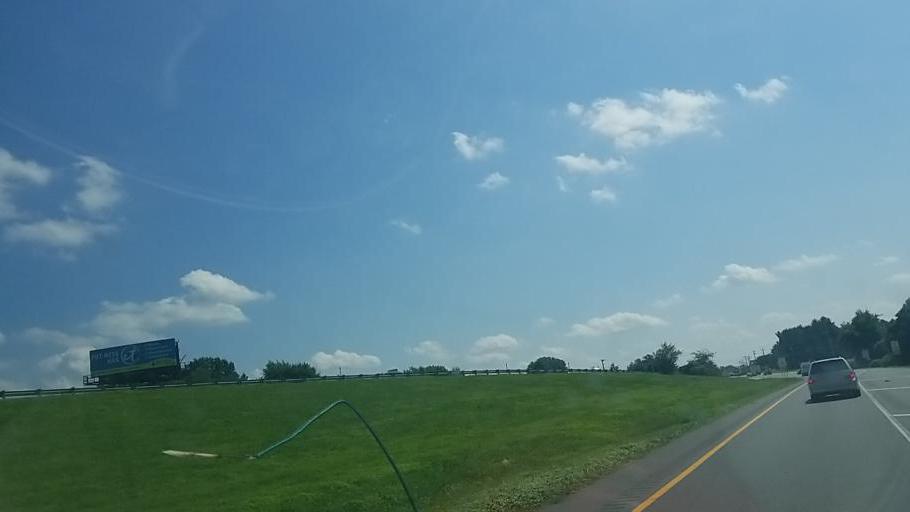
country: US
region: Delaware
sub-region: Sussex County
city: Milford
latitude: 38.9374
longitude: -75.4285
